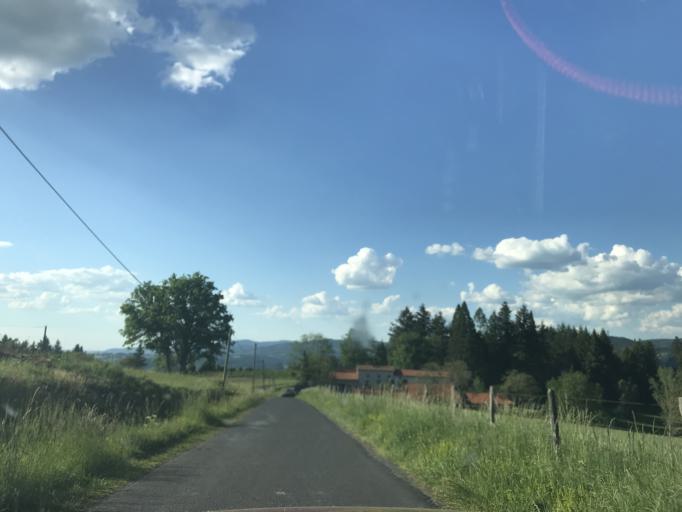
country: FR
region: Auvergne
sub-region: Departement du Puy-de-Dome
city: Job
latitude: 45.6248
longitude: 3.6783
